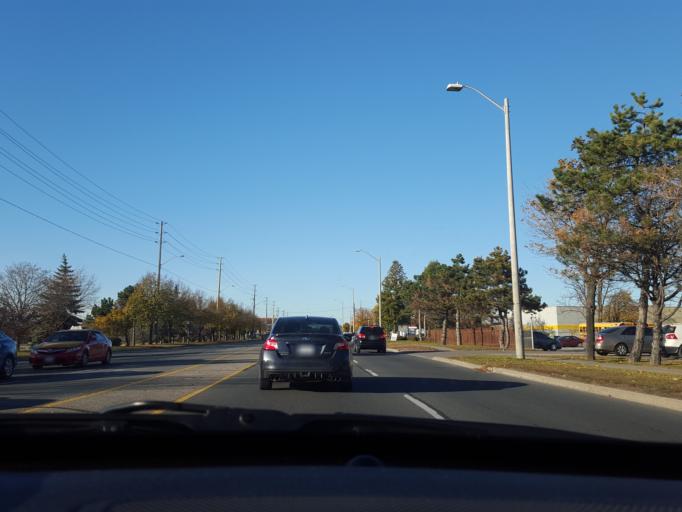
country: CA
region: Ontario
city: Markham
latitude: 43.8703
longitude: -79.2852
